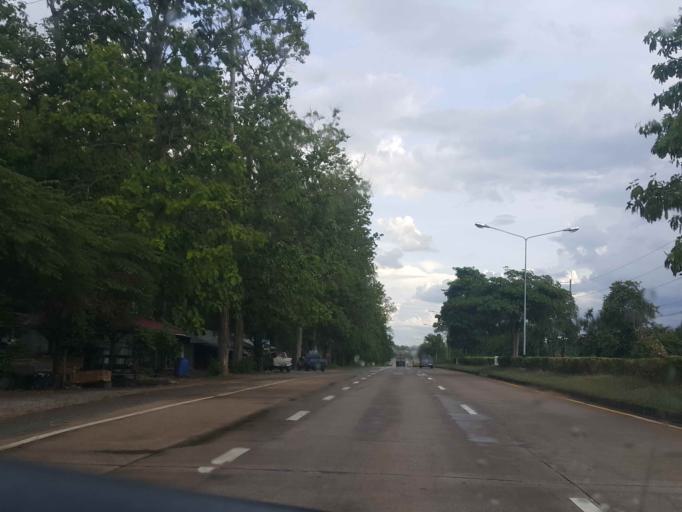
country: TH
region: Phrae
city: Den Chai
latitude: 17.9873
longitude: 100.0957
